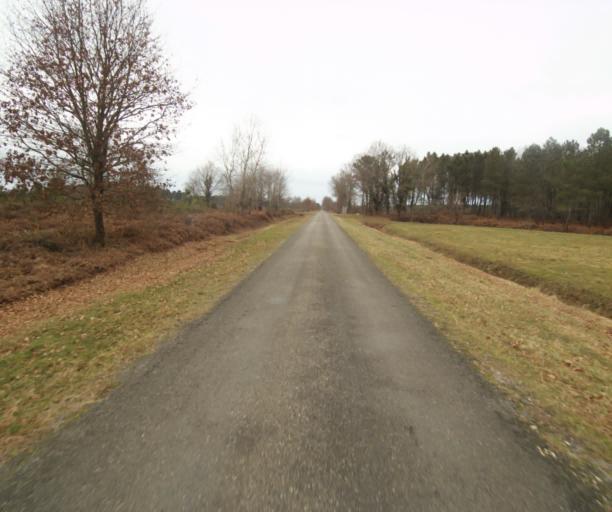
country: FR
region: Aquitaine
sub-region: Departement des Landes
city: Gabarret
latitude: 44.0380
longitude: -0.0732
